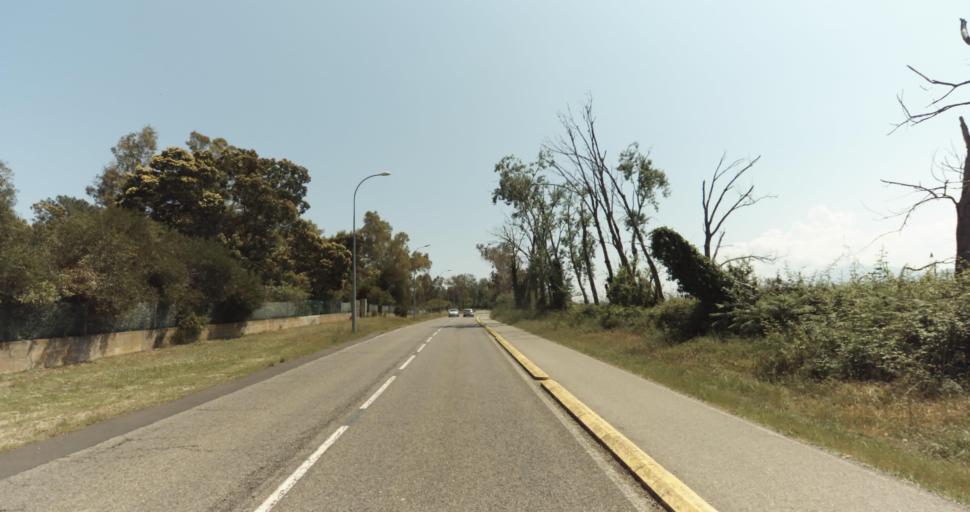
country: FR
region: Corsica
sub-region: Departement de la Haute-Corse
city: Biguglia
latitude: 42.6273
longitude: 9.4682
